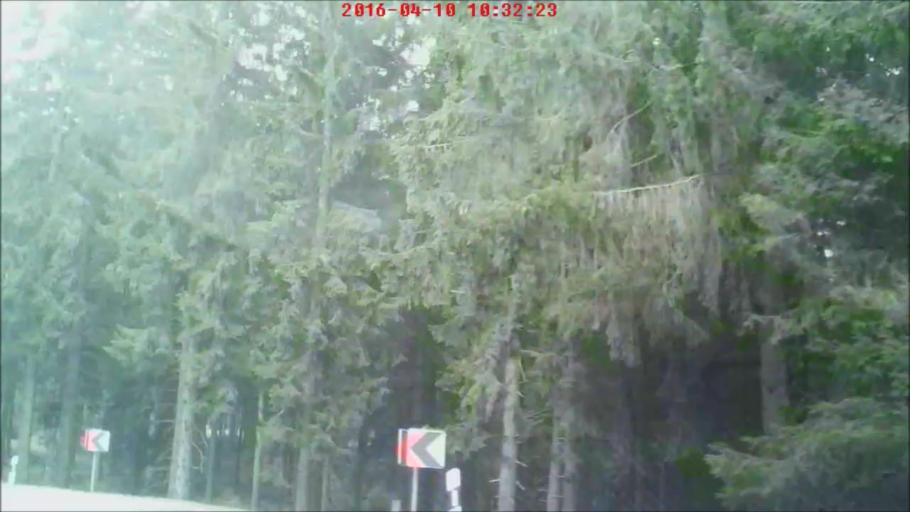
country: DE
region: Thuringia
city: Stutzerbach
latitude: 50.6072
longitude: 10.8784
